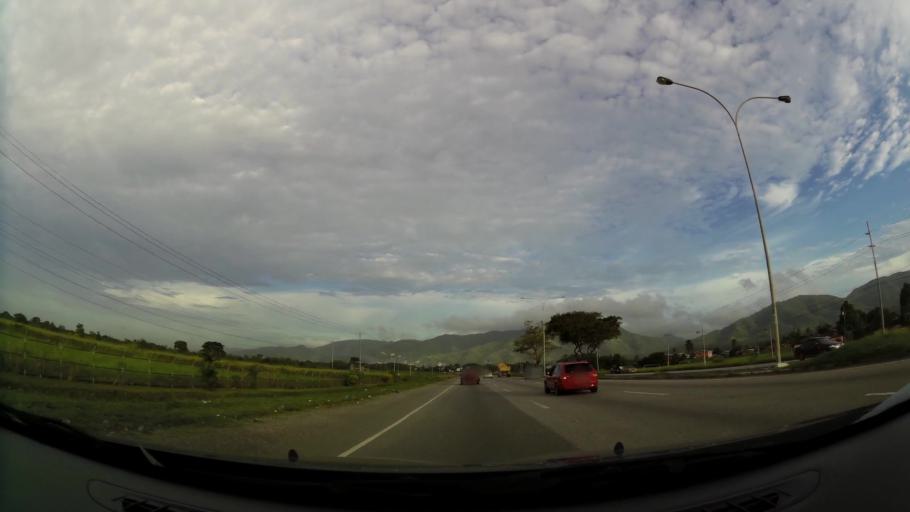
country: TT
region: Tunapuna/Piarco
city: Tunapuna
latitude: 10.6294
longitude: -61.3601
